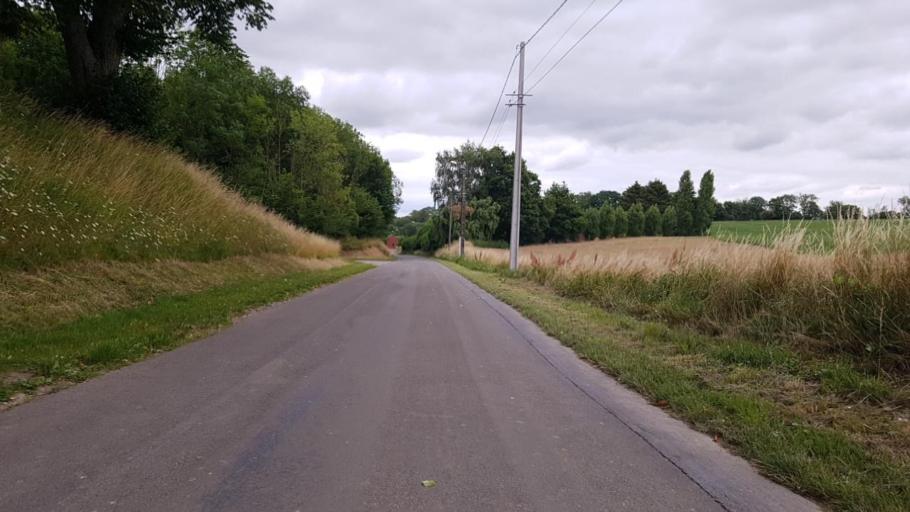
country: FR
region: Picardie
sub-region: Departement de l'Aisne
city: Guise
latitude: 49.8955
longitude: 3.6147
